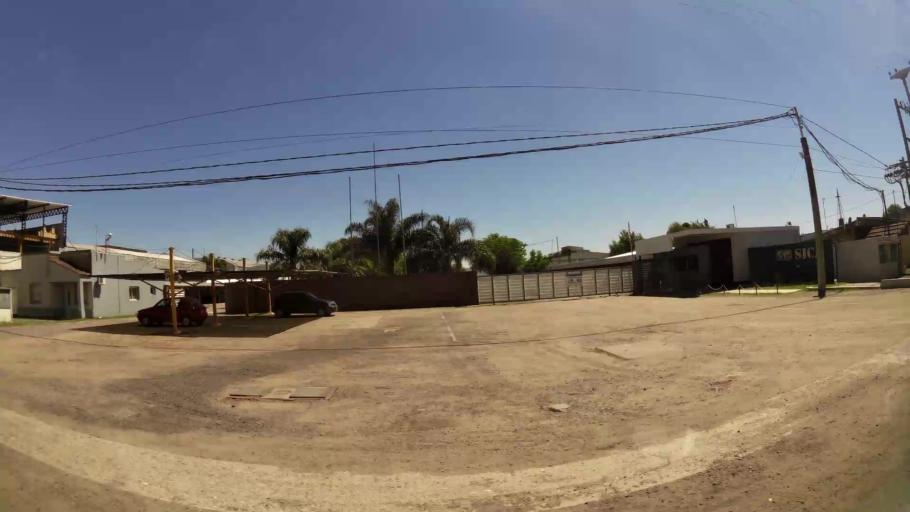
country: AR
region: Santa Fe
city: Esperanza
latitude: -31.4378
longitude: -60.9499
